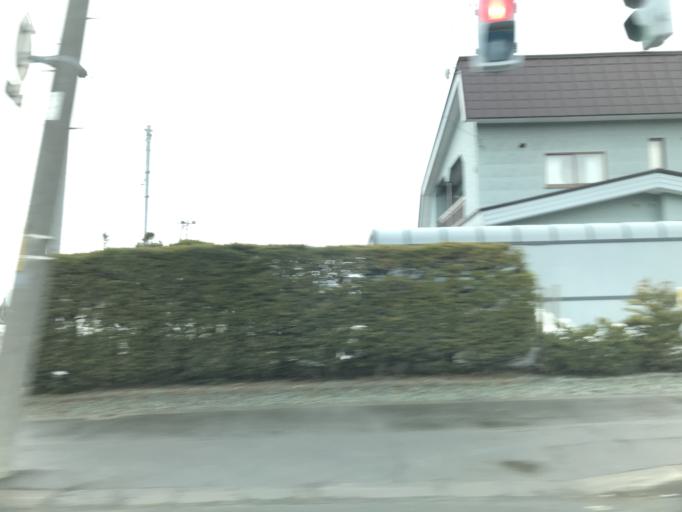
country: JP
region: Hokkaido
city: Nayoro
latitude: 44.2360
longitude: 142.3947
